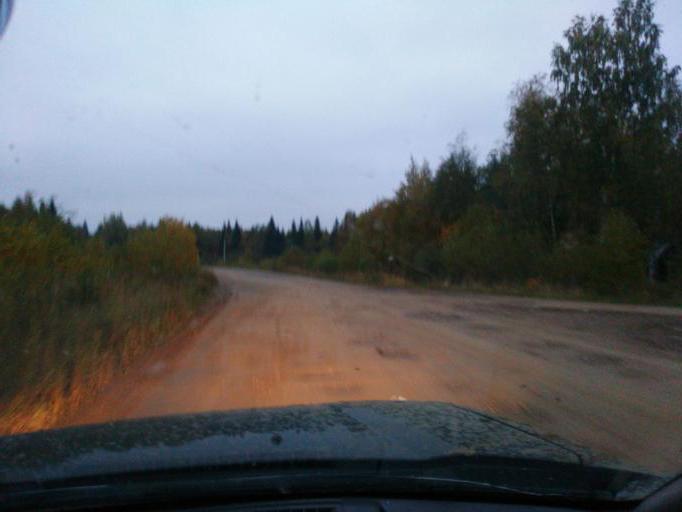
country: RU
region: Perm
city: Gornozavodsk
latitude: 57.8820
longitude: 58.4289
